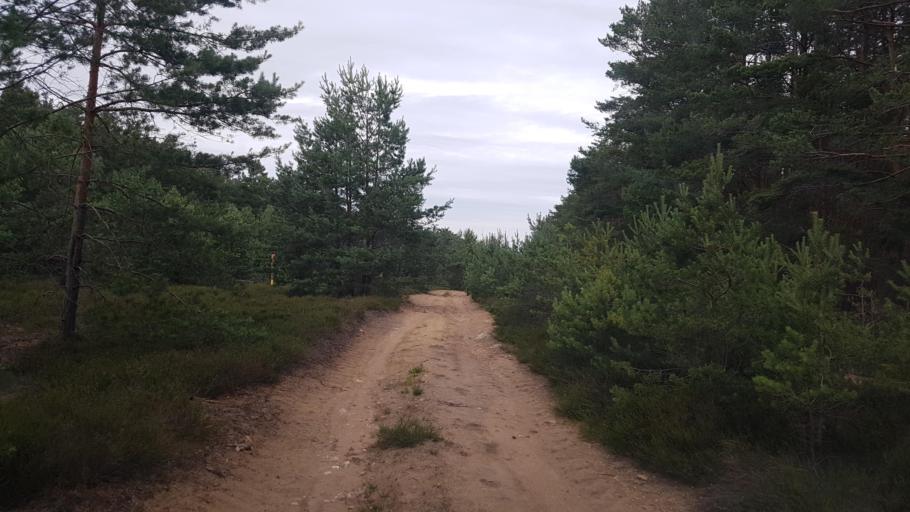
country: DE
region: Brandenburg
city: Treuenbrietzen
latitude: 52.0547
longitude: 12.8109
